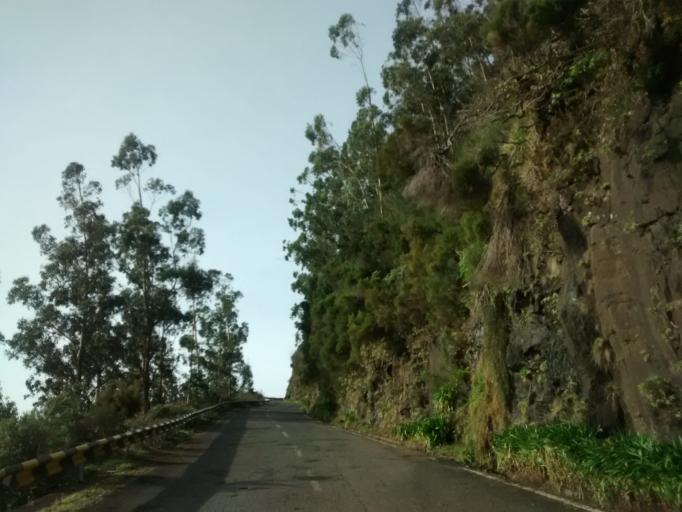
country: PT
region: Madeira
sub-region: Sao Vicente
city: Sao Vicente
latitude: 32.7507
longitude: -17.0308
